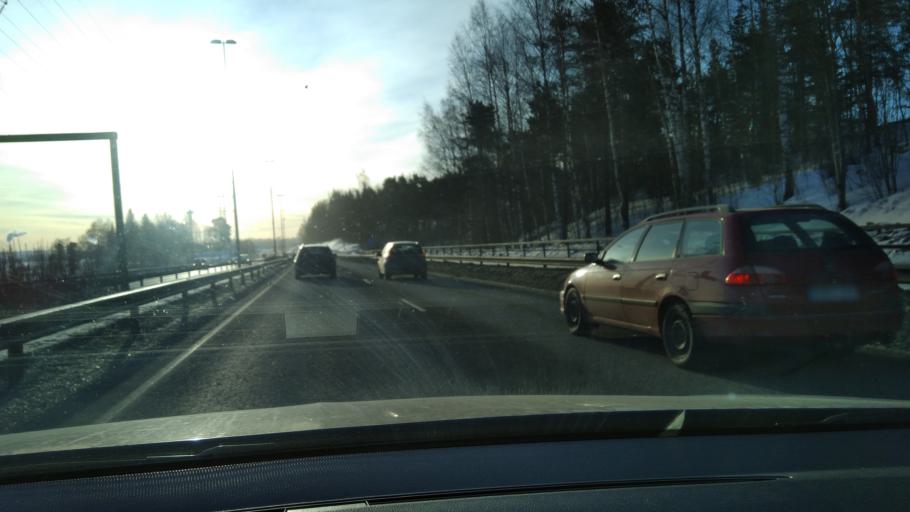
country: FI
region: Pirkanmaa
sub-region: Tampere
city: Pirkkala
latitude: 61.5088
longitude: 23.6956
